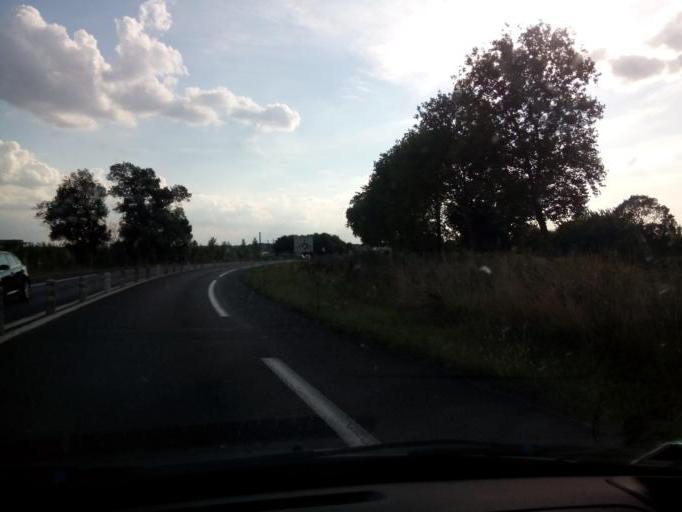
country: FR
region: Centre
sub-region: Departement d'Indre-et-Loire
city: Savonnieres
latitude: 47.3024
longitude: 0.5568
